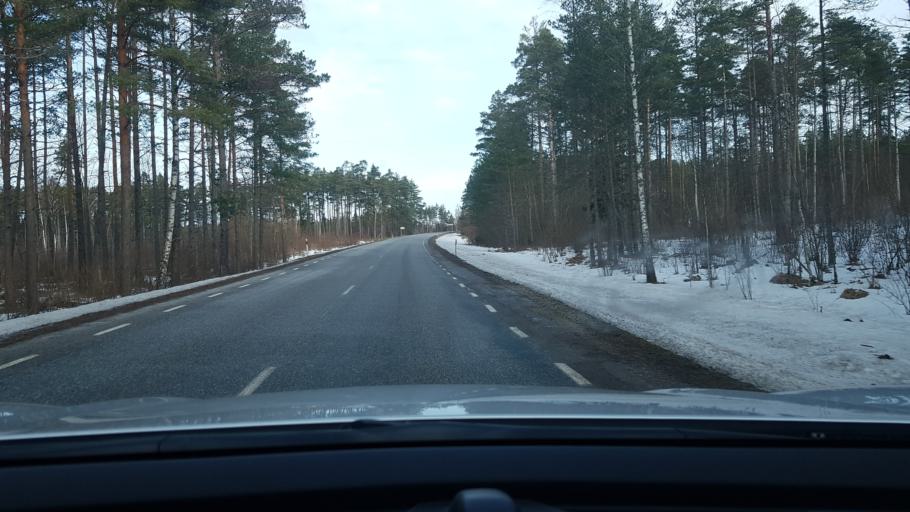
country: EE
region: Saare
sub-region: Kuressaare linn
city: Kuressaare
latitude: 58.4392
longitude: 22.7048
